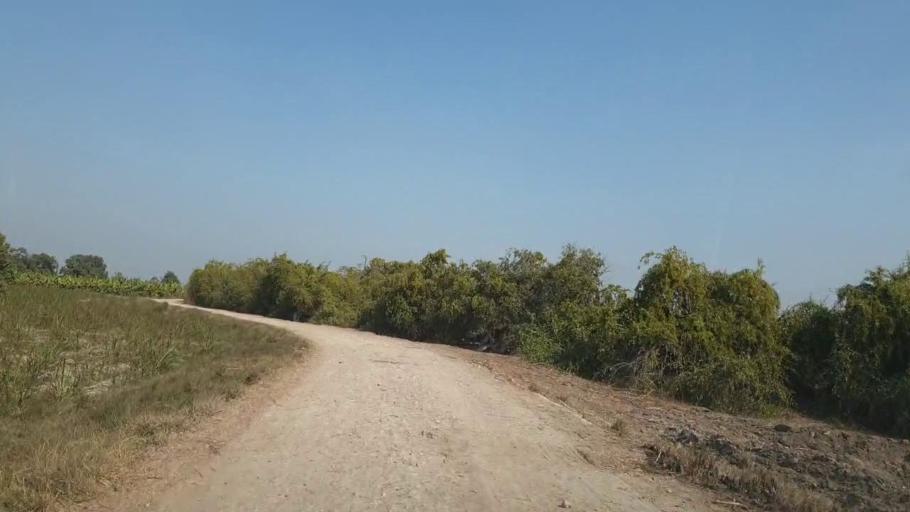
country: PK
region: Sindh
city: Matiari
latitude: 25.5021
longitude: 68.4693
